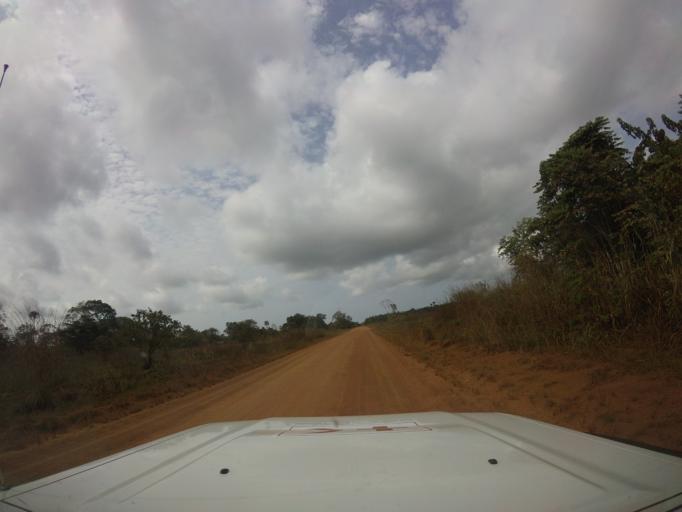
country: LR
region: Grand Cape Mount
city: Robertsport
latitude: 6.6757
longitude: -11.1393
